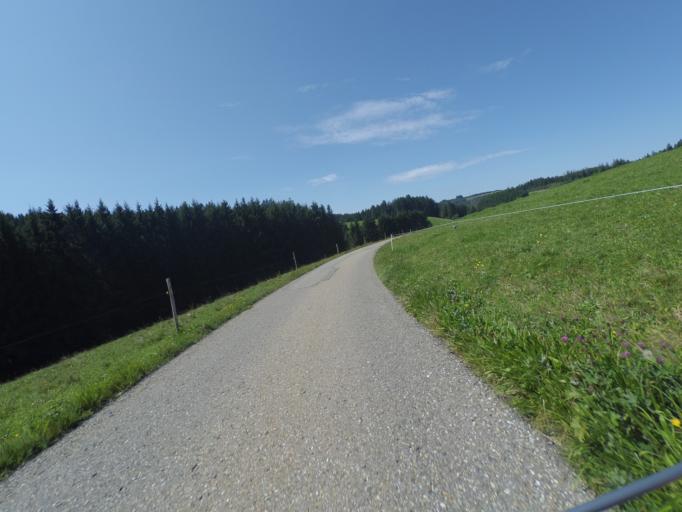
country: DE
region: Baden-Wuerttemberg
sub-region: Freiburg Region
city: Gutenbach
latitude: 48.0471
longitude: 8.1588
